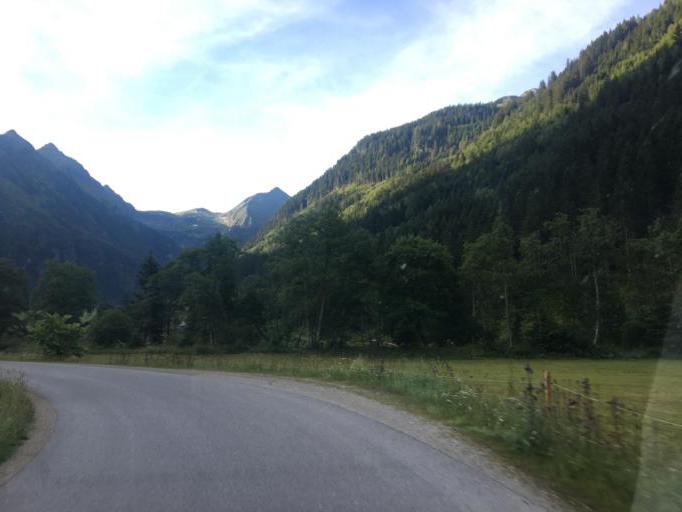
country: AT
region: Styria
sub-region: Politischer Bezirk Liezen
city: Haus
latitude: 47.3340
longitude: 13.7471
